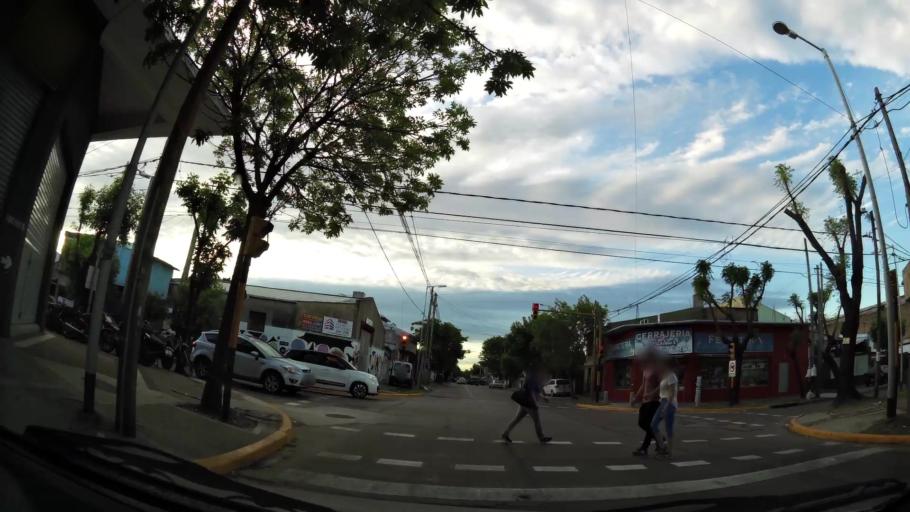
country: AR
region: Buenos Aires
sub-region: Partido de Avellaneda
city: Avellaneda
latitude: -34.6942
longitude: -58.3476
